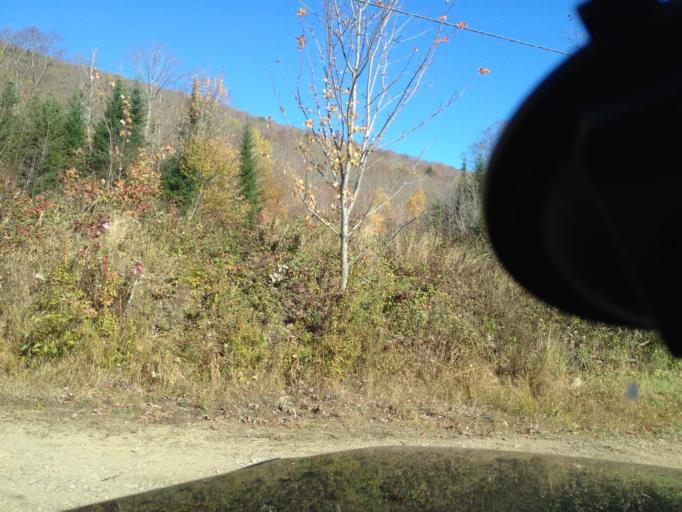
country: CA
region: Quebec
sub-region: Laurentides
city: Val-David
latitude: 46.2979
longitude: -74.1079
